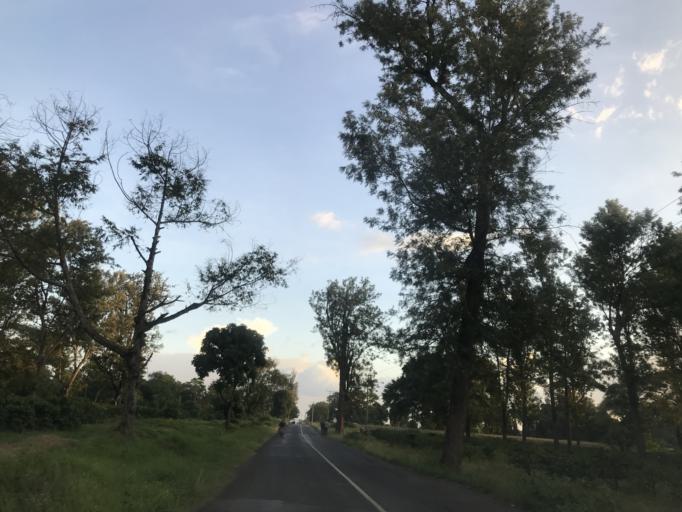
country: TZ
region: Arusha
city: Usa River
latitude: -3.3570
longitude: 36.8659
